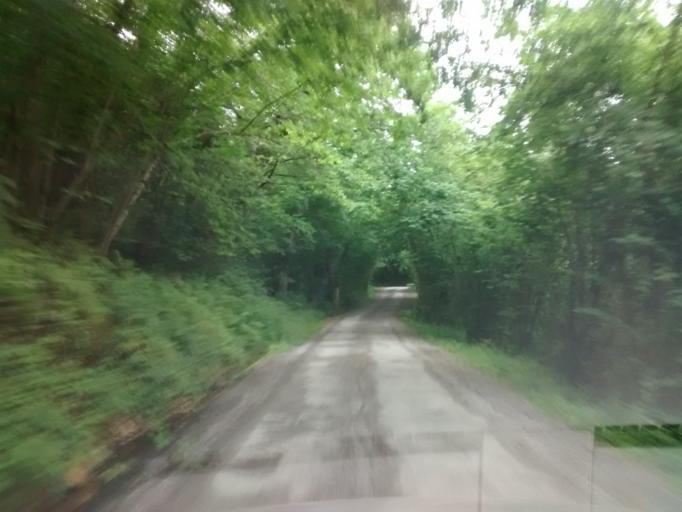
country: ES
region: Asturias
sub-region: Province of Asturias
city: Pilona
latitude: 43.2737
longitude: -5.3486
